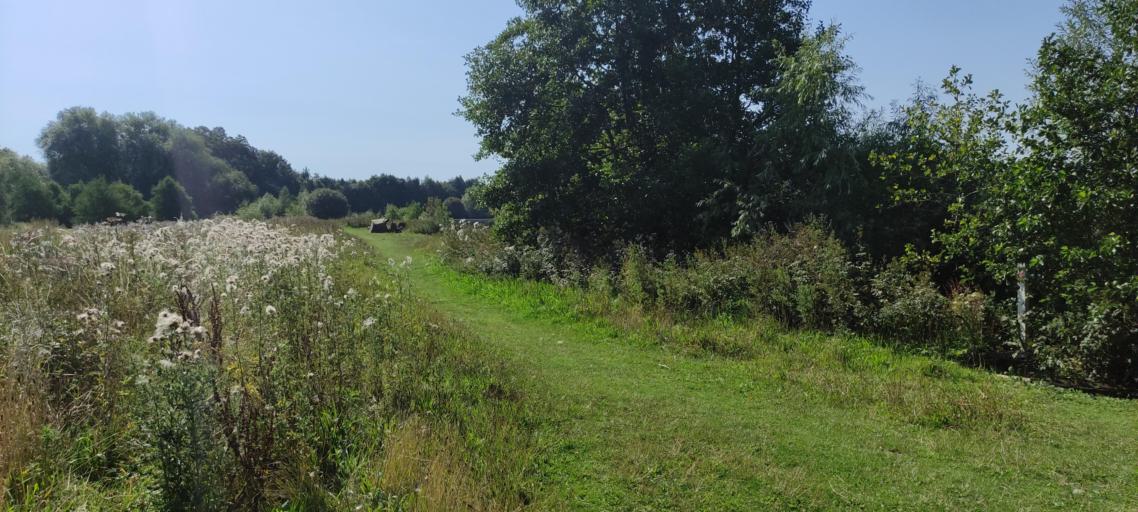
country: GB
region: England
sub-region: North Yorkshire
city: Catterick
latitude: 54.3723
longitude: -1.5809
